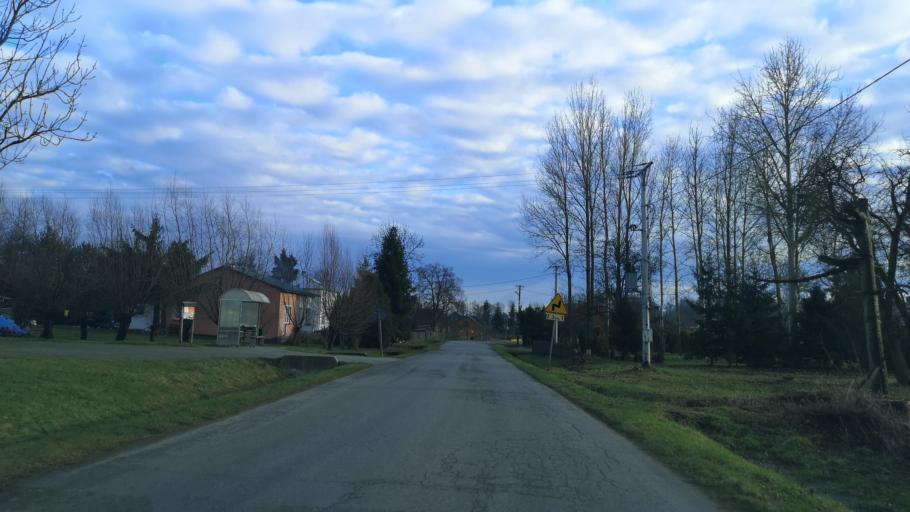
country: PL
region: Subcarpathian Voivodeship
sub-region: Powiat lezajski
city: Piskorowice
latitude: 50.2624
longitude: 22.5928
